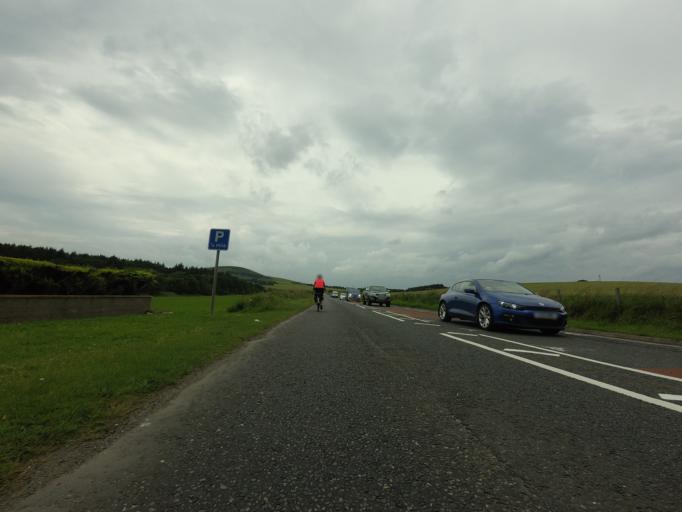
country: GB
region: Scotland
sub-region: Aberdeenshire
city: Portsoy
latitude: 57.6783
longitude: -2.7001
